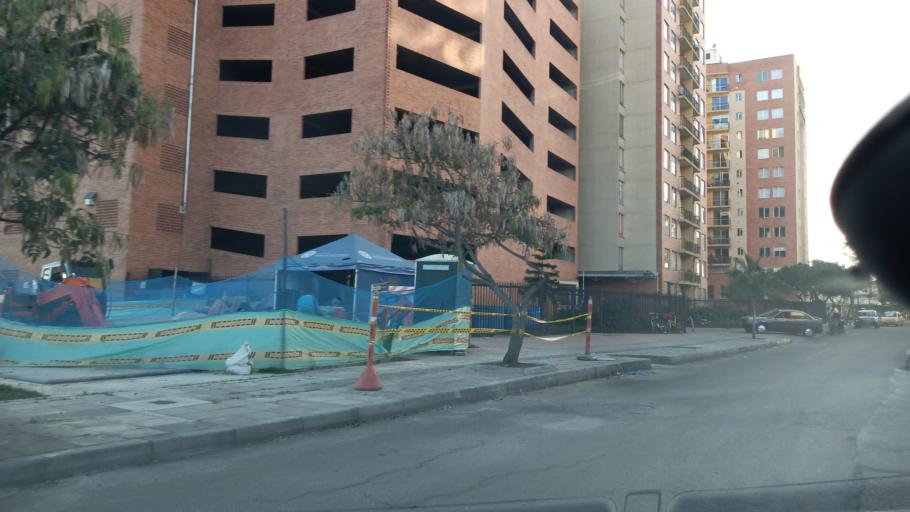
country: CO
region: Bogota D.C.
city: Bogota
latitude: 4.6341
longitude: -74.1253
